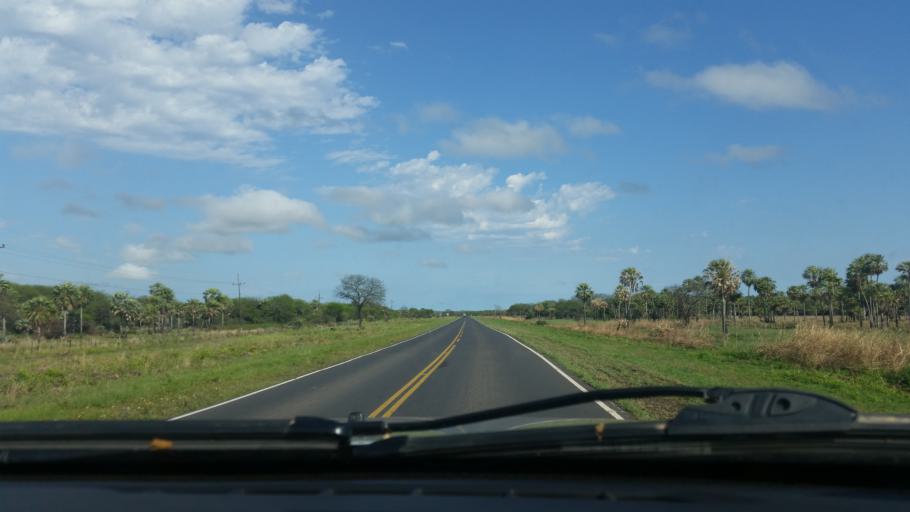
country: PY
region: Presidente Hayes
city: Benjamin Aceval
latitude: -24.9103
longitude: -57.6318
